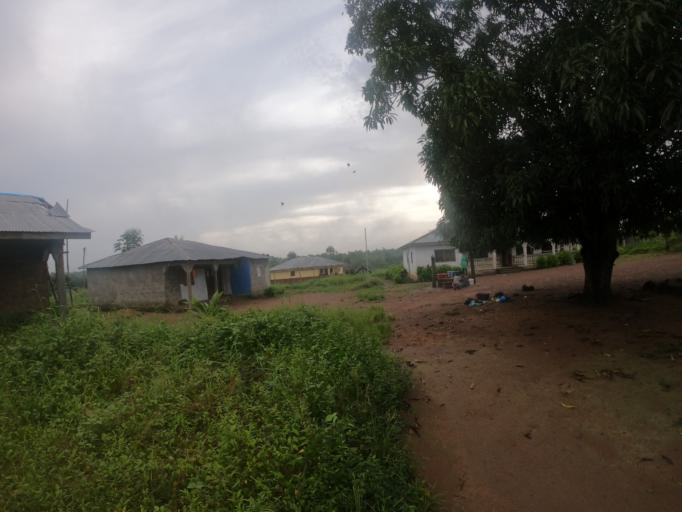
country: SL
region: Northern Province
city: Port Loko
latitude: 8.4951
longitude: -12.7500
